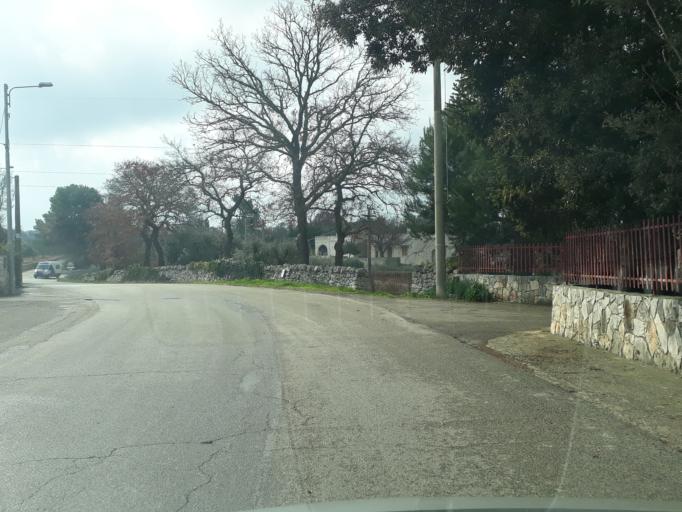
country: IT
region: Apulia
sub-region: Provincia di Brindisi
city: Lamie di Olimpie-Selva
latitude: 40.7947
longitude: 17.3426
